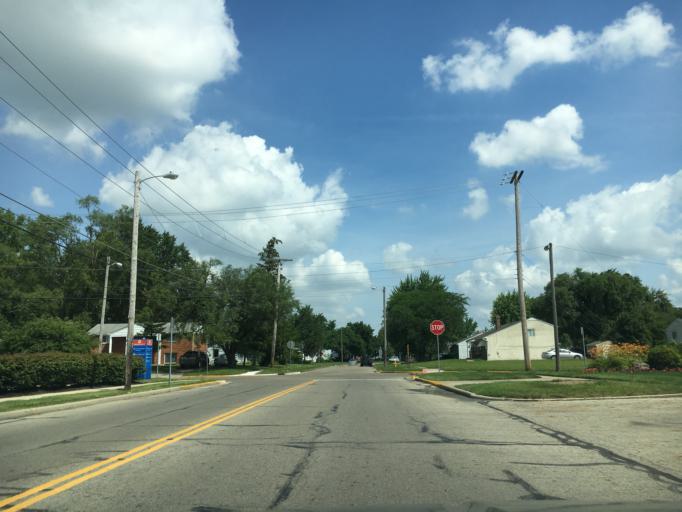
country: US
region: Ohio
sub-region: Franklin County
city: Lincoln Village
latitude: 39.9540
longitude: -83.1362
